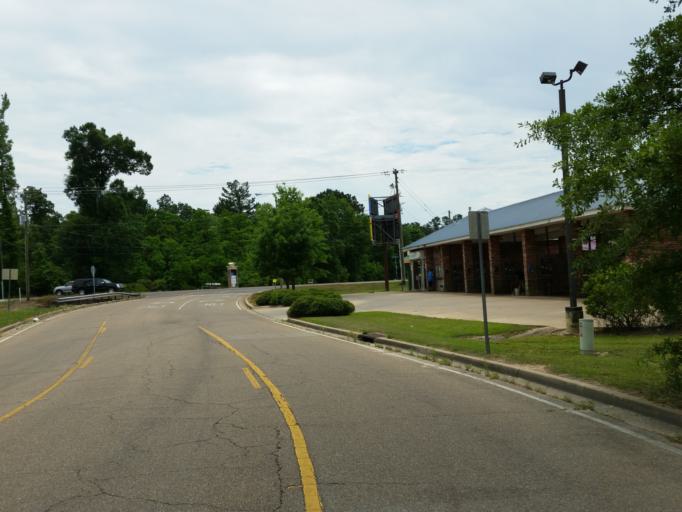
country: US
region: Mississippi
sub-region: Lamar County
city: West Hattiesburg
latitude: 31.3192
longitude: -89.3623
